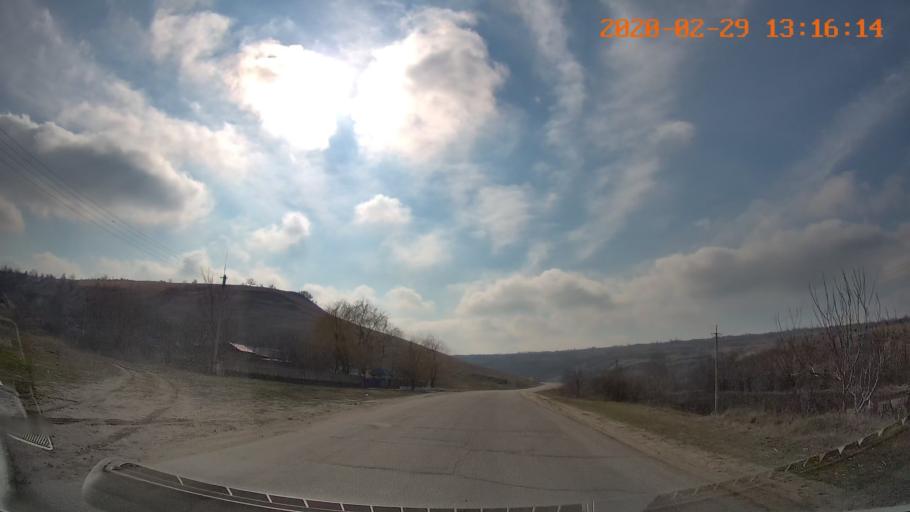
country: MD
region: Telenesti
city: Camenca
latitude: 48.0040
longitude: 28.6660
